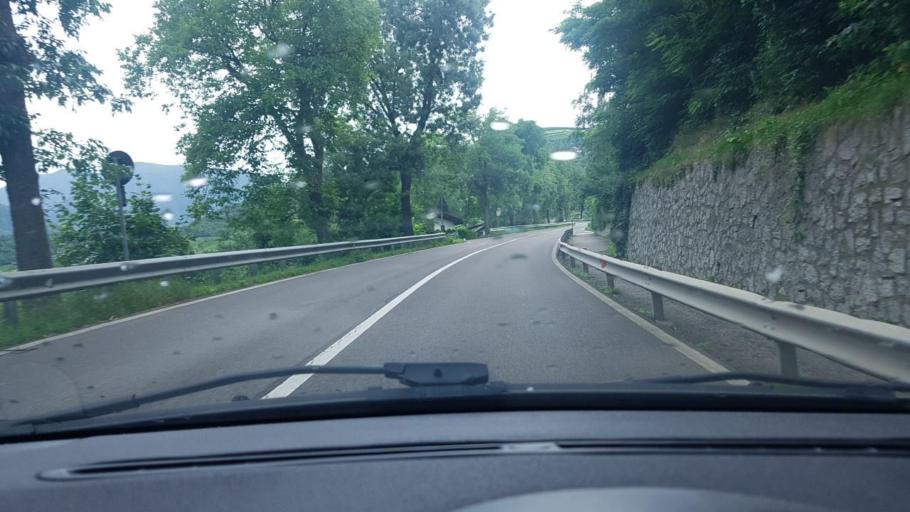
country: IT
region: Trentino-Alto Adige
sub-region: Bolzano
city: Leone-Santa Elisabetta
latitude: 46.7383
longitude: 11.6512
